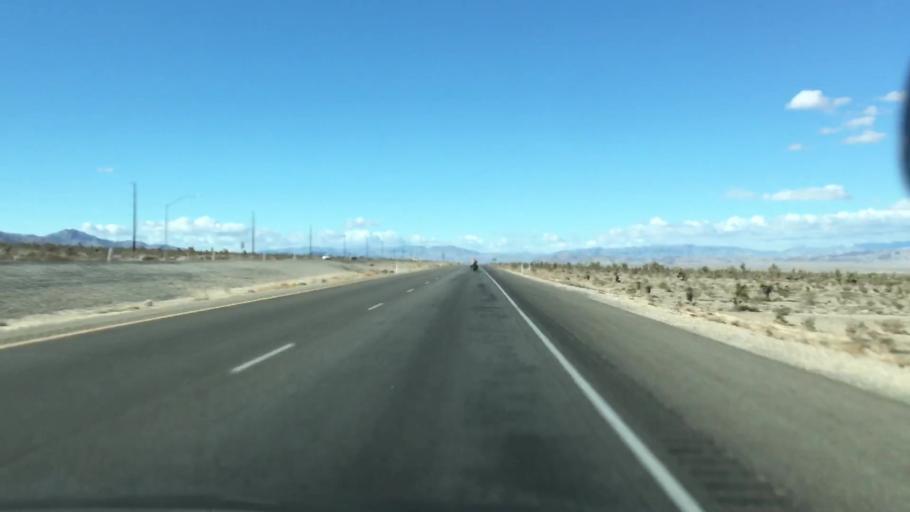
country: US
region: Nevada
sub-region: Clark County
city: Summerlin South
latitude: 36.4790
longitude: -115.4701
